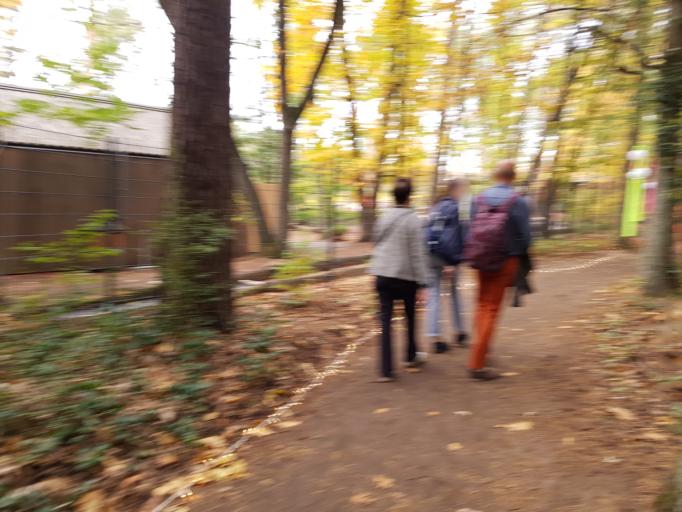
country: DE
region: Brandenburg
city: Fichtenwalde
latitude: 52.2630
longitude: 12.9170
